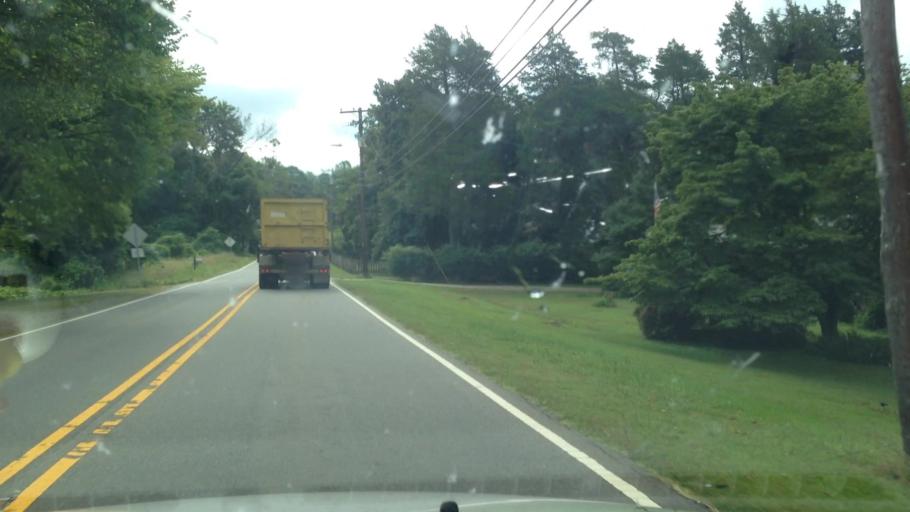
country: US
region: North Carolina
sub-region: Rockingham County
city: Wentworth
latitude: 36.3980
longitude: -79.7691
